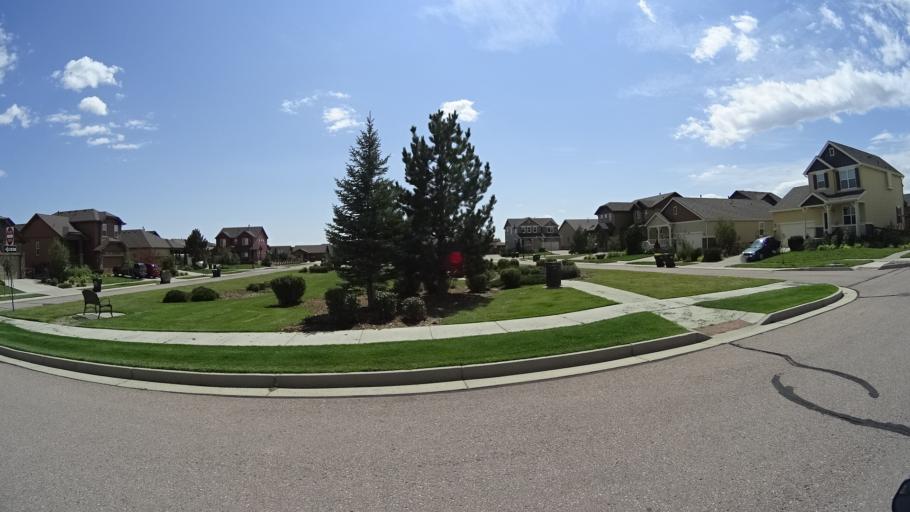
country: US
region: Colorado
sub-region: El Paso County
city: Cimarron Hills
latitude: 38.9328
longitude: -104.6796
